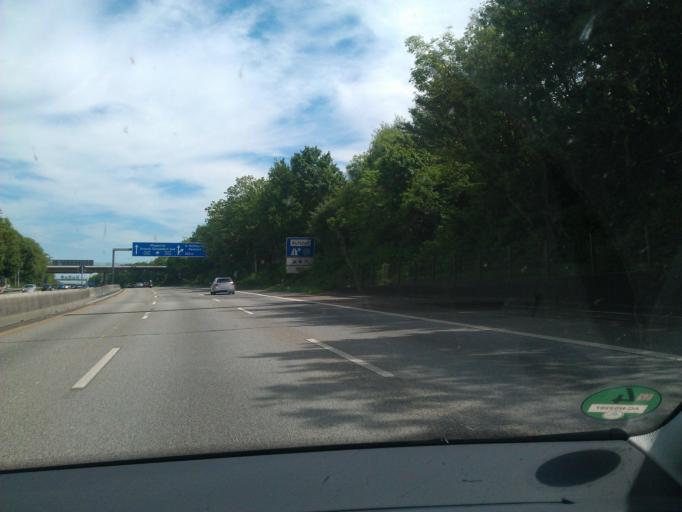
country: DE
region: North Rhine-Westphalia
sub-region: Regierungsbezirk Dusseldorf
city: Dusseldorf
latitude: 51.1932
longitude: 6.8176
